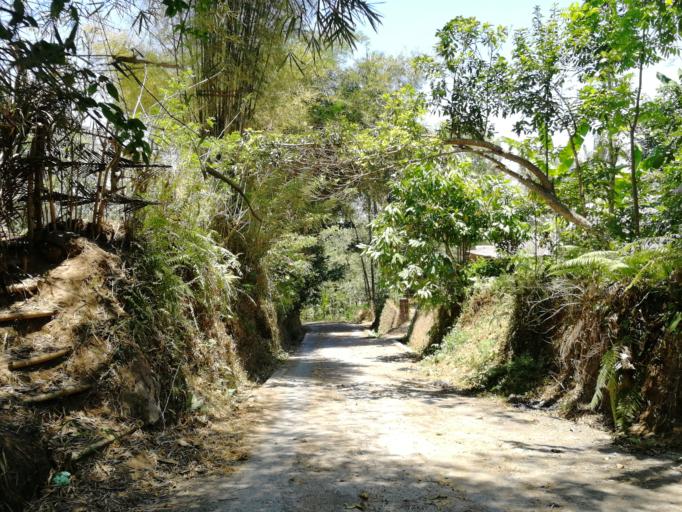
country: ID
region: West Nusa Tenggara
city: Tetebatu
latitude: -8.5500
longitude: 116.4193
